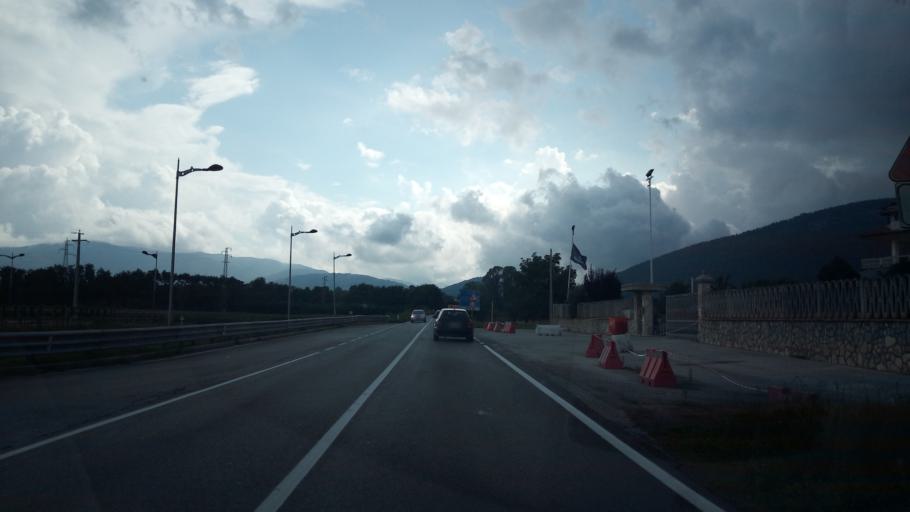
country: IT
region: Campania
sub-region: Provincia di Salerno
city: Buonabitacolo
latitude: 40.2884
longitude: 15.6399
